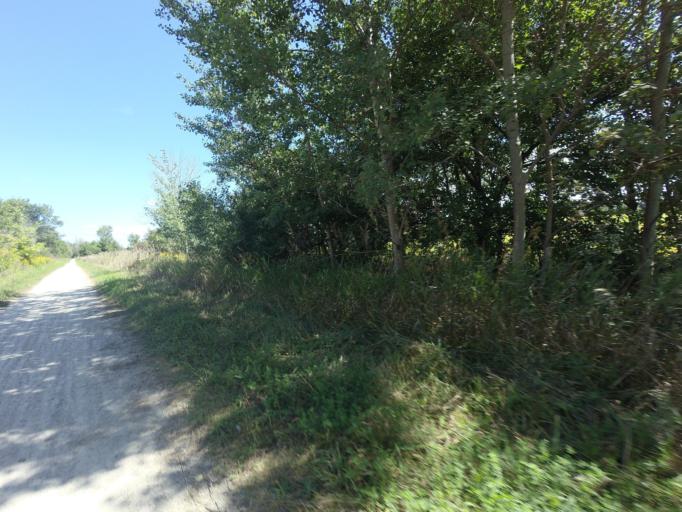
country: CA
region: Ontario
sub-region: Wellington County
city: Guelph
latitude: 43.7309
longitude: -80.3689
